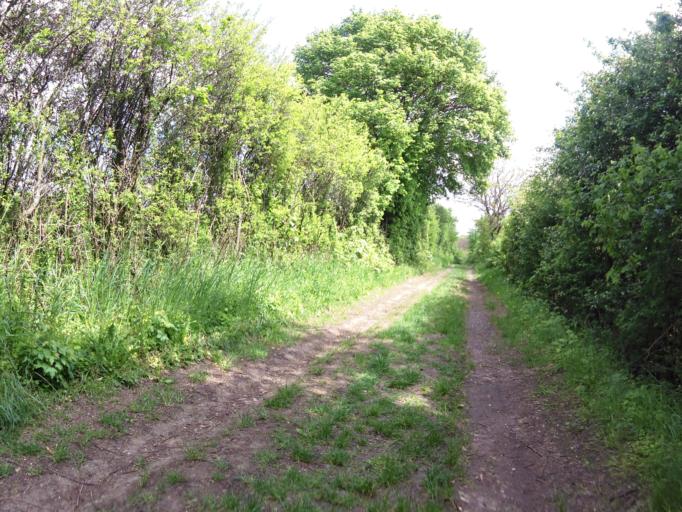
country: DE
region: Bavaria
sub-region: Regierungsbezirk Unterfranken
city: Reichenberg
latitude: 49.7341
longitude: 9.9114
